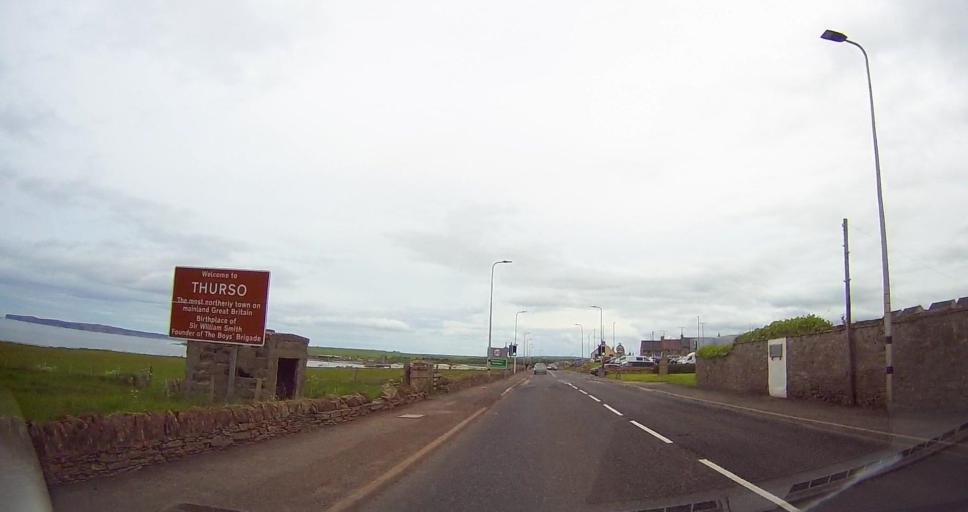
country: GB
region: Scotland
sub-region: Highland
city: Thurso
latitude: 58.5981
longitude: -3.5348
